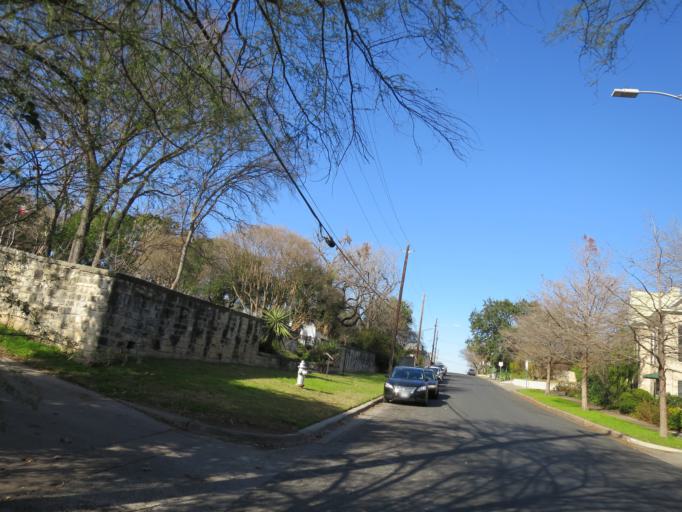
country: US
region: Texas
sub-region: Travis County
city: Austin
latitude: 30.2663
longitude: -97.7317
